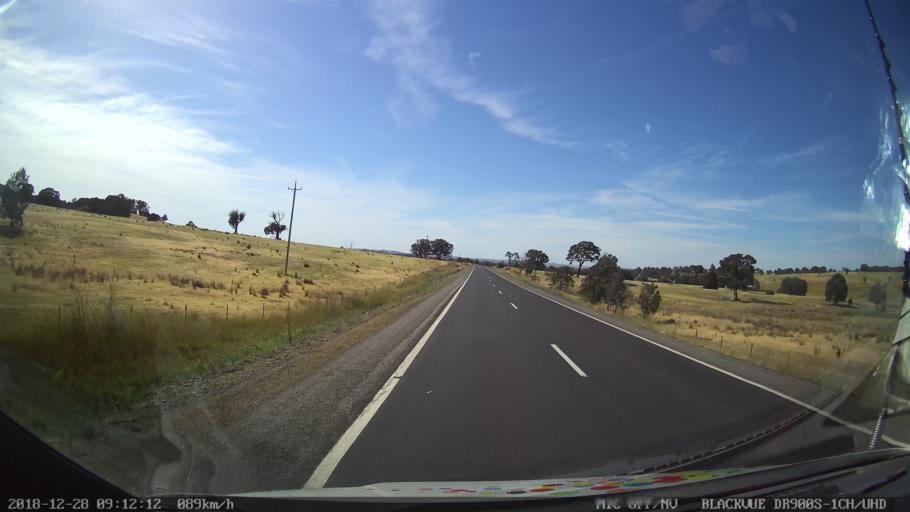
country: AU
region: New South Wales
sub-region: Upper Lachlan Shire
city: Crookwell
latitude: -34.2525
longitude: 149.3399
